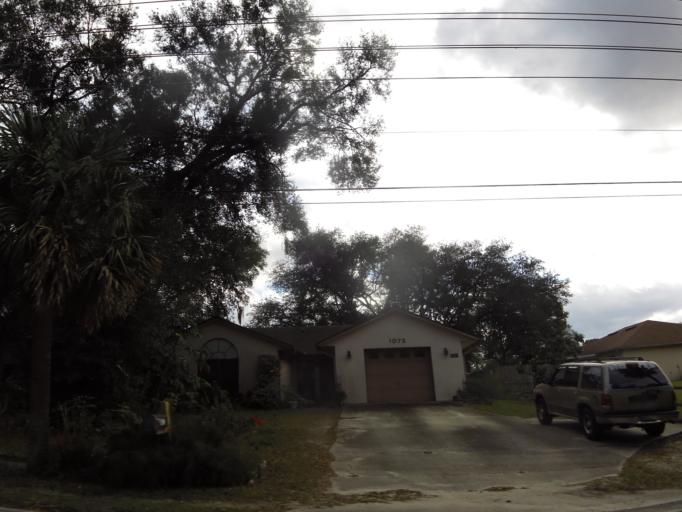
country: US
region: Florida
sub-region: Volusia County
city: Orange City
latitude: 28.9486
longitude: -81.2859
